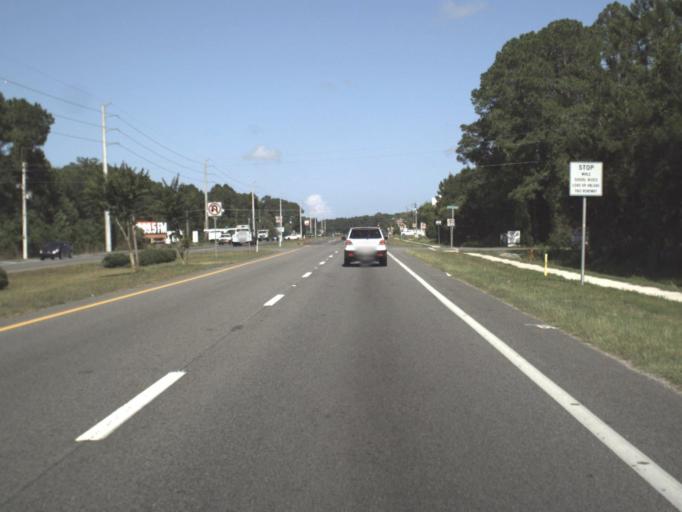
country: US
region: Florida
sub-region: Saint Johns County
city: Saint Augustine
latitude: 29.9160
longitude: -81.4057
